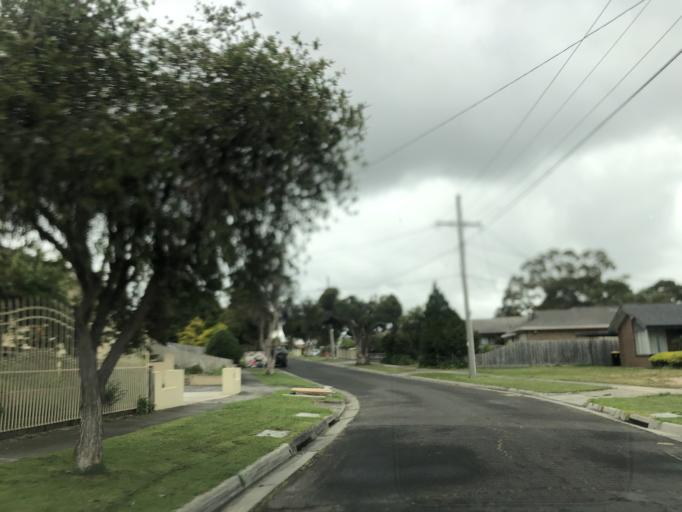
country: AU
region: Victoria
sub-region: Greater Dandenong
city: Dandenong North
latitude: -37.9588
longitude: 145.2162
